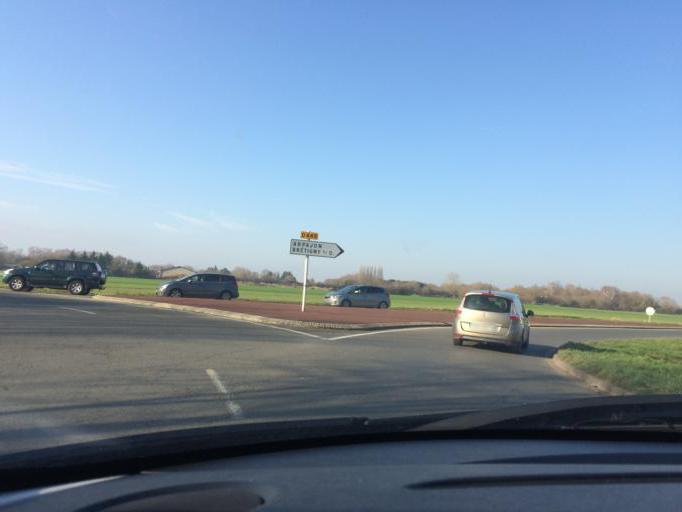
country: FR
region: Ile-de-France
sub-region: Departement de l'Essonne
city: La Norville
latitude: 48.5657
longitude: 2.2621
